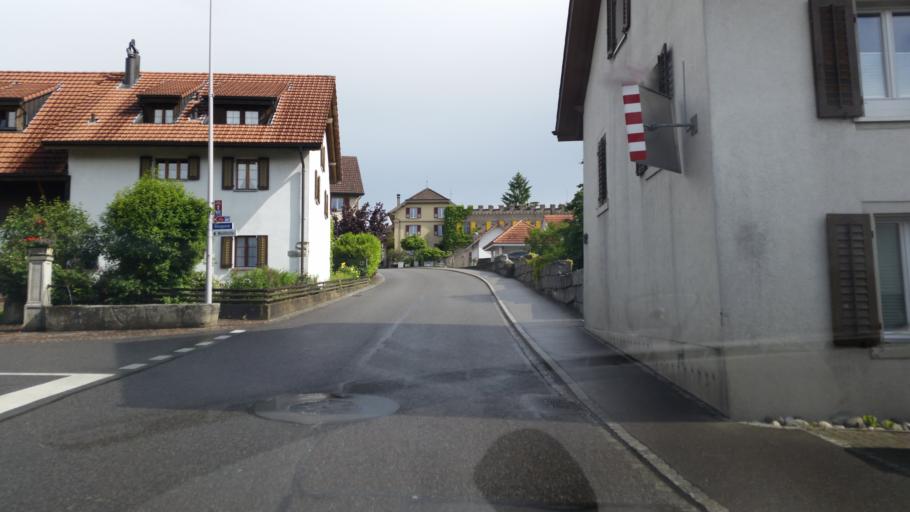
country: CH
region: Aargau
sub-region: Bezirk Lenzburg
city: Seengen
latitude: 47.3221
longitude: 8.2086
